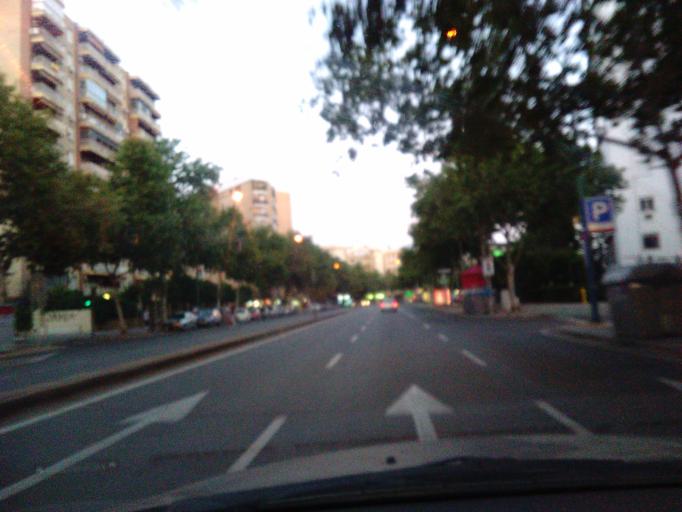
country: ES
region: Andalusia
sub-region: Provincia de Sevilla
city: Sevilla
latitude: 37.3895
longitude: -5.9743
